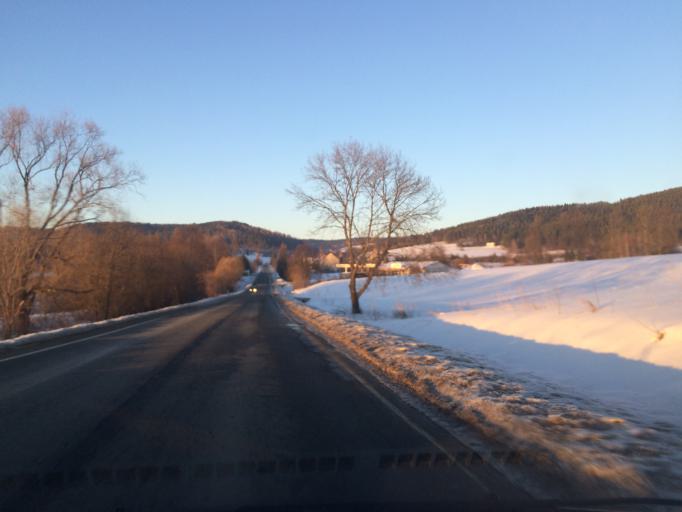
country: PL
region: Subcarpathian Voivodeship
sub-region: Powiat bieszczadzki
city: Czarna
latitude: 49.3303
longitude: 22.6703
